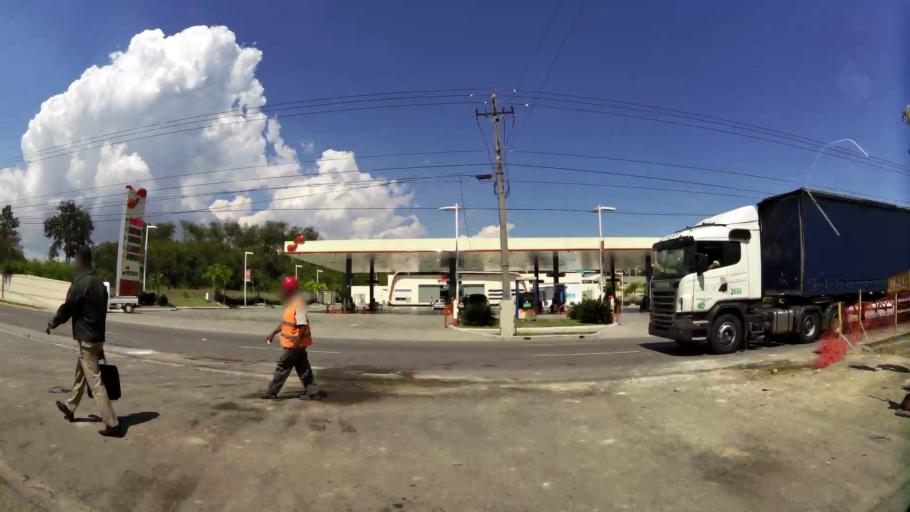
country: DO
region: Nacional
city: Bella Vista
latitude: 18.4569
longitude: -69.9829
